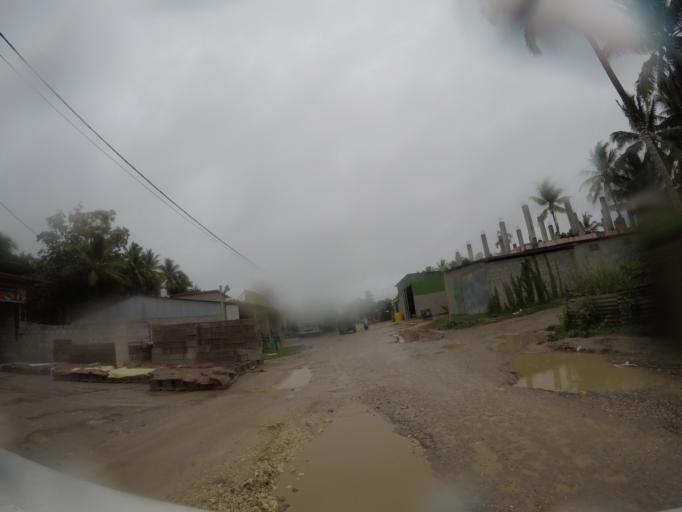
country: TL
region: Lautem
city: Lospalos
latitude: -8.5169
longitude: 126.9998
